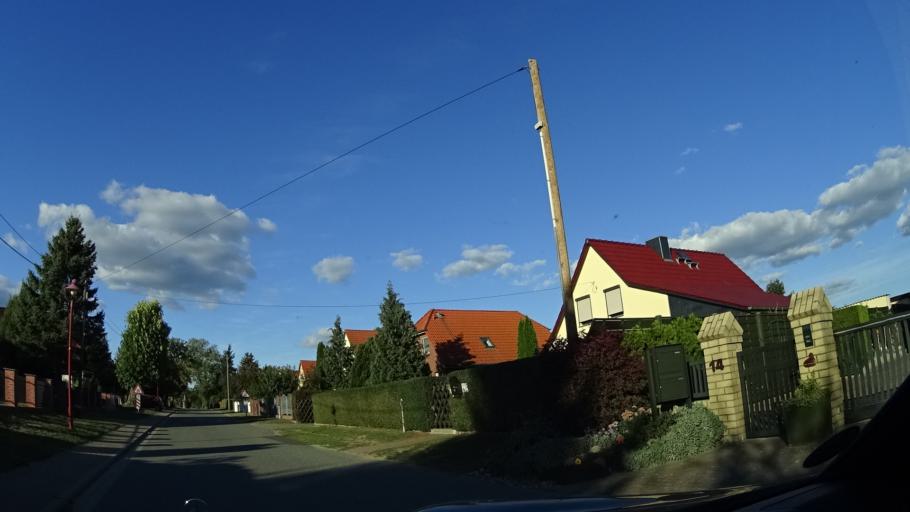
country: DE
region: Brandenburg
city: Dabergotz
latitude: 52.9321
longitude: 12.7464
